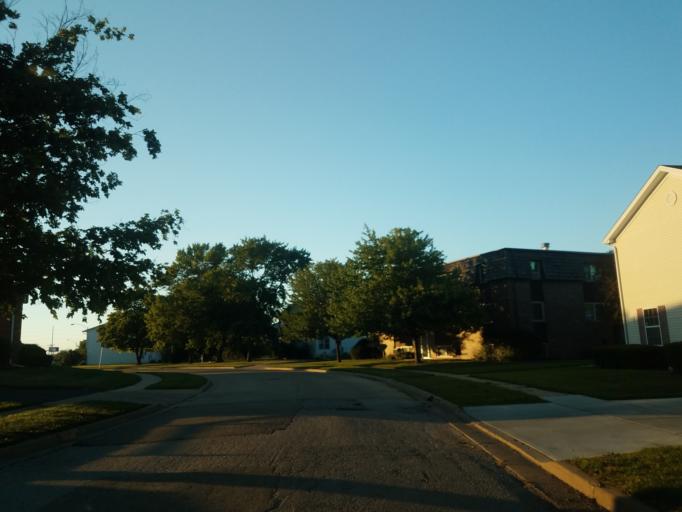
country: US
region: Illinois
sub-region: McLean County
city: Bloomington
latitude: 40.4709
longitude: -88.9496
